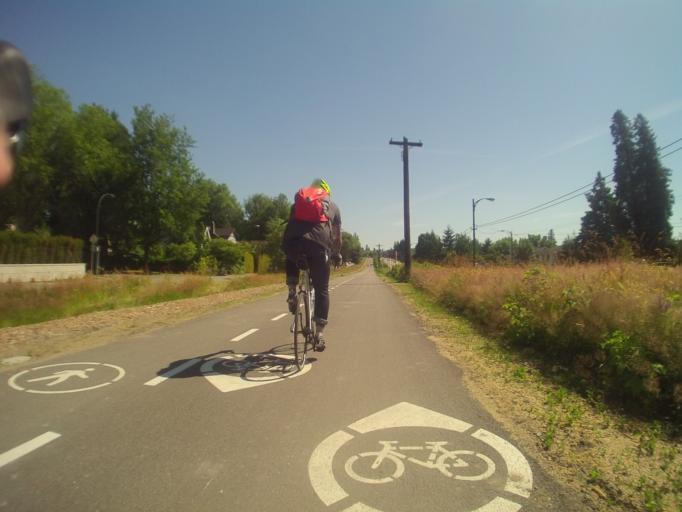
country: CA
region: British Columbia
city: West End
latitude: 49.2566
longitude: -123.1529
